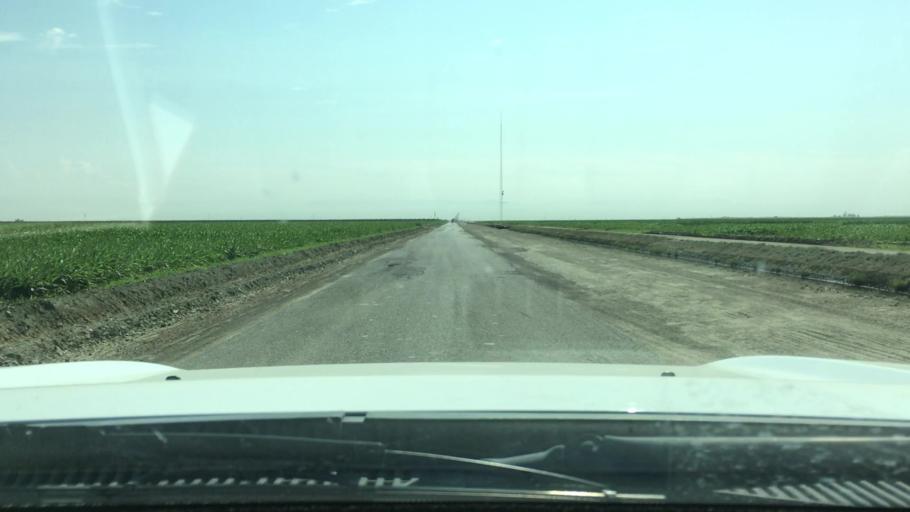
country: US
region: California
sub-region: Kings County
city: Corcoran
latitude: 36.0072
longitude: -119.5293
